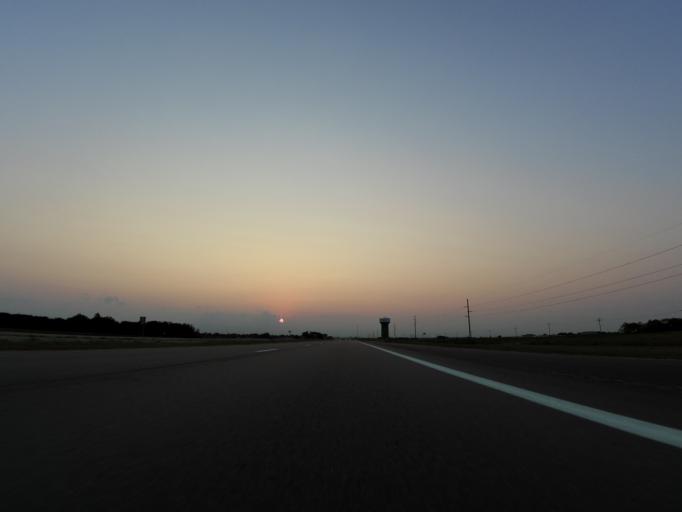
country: US
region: Kansas
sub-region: Reno County
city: South Hutchinson
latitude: 38.0132
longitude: -97.9519
